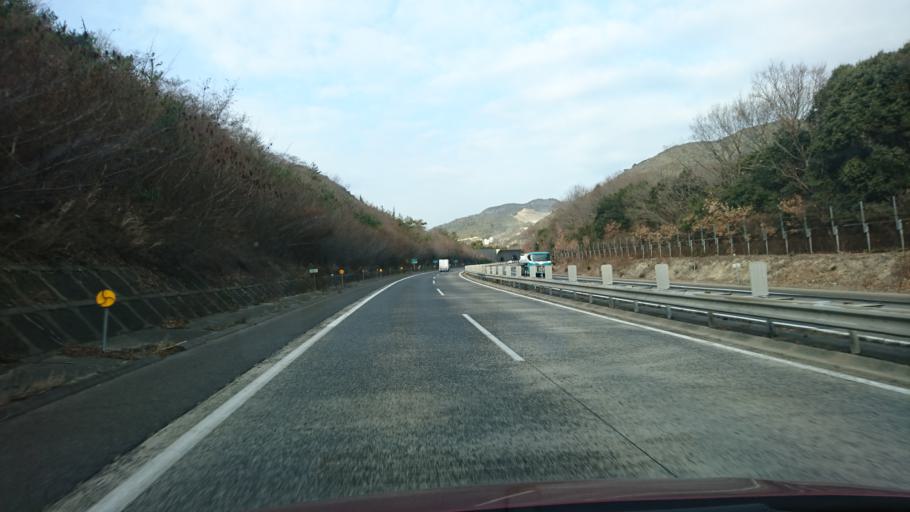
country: JP
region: Hyogo
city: Kariya
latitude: 34.7769
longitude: 134.3500
